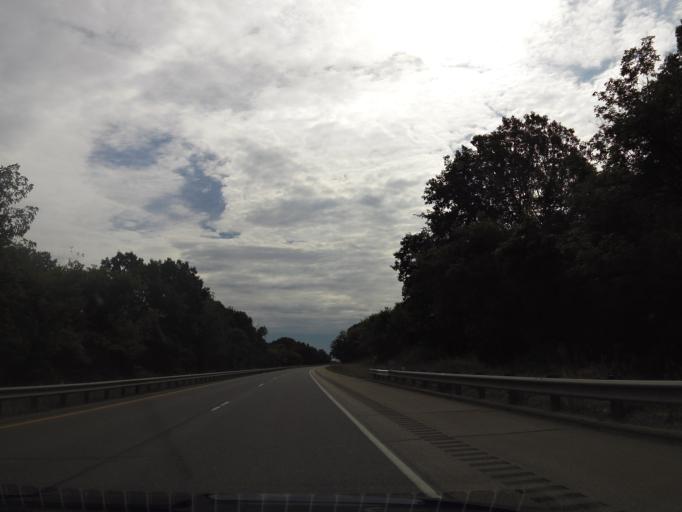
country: US
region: Wisconsin
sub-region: La Crosse County
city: Brice Prairie
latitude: 43.9194
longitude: -91.3796
